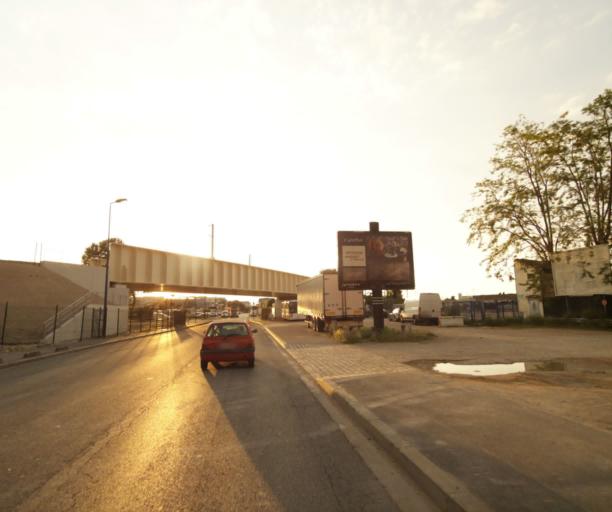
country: FR
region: Ile-de-France
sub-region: Departement des Hauts-de-Seine
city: Gennevilliers
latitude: 48.9292
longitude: 2.3103
